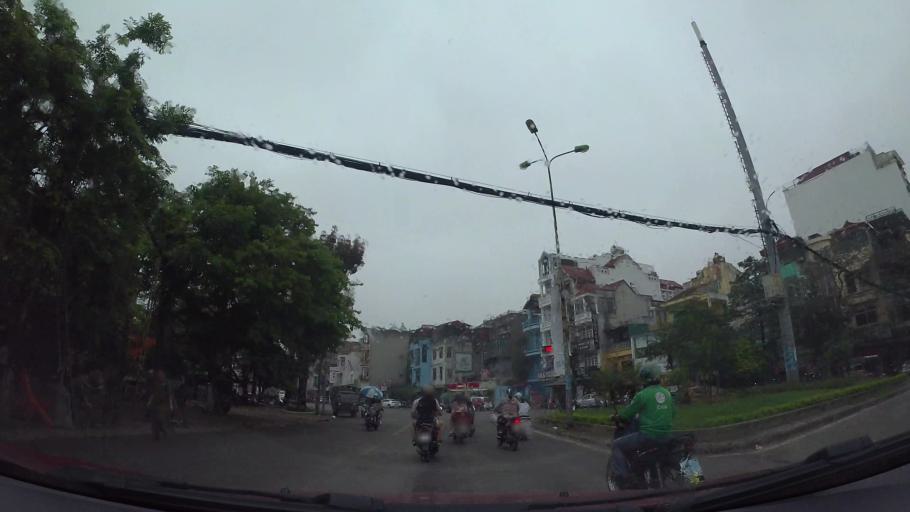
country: VN
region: Ha Noi
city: Dong Da
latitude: 21.0113
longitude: 105.8310
